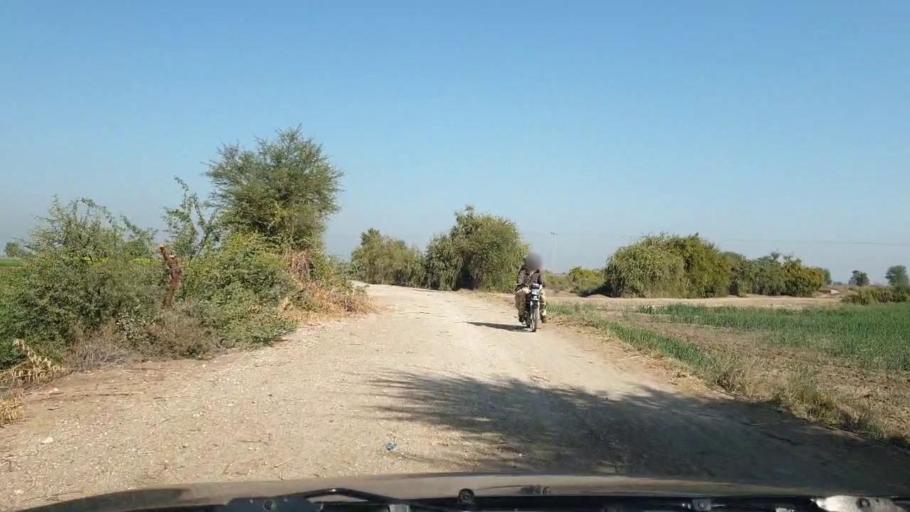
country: PK
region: Sindh
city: Jhol
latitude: 25.9549
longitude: 68.8217
